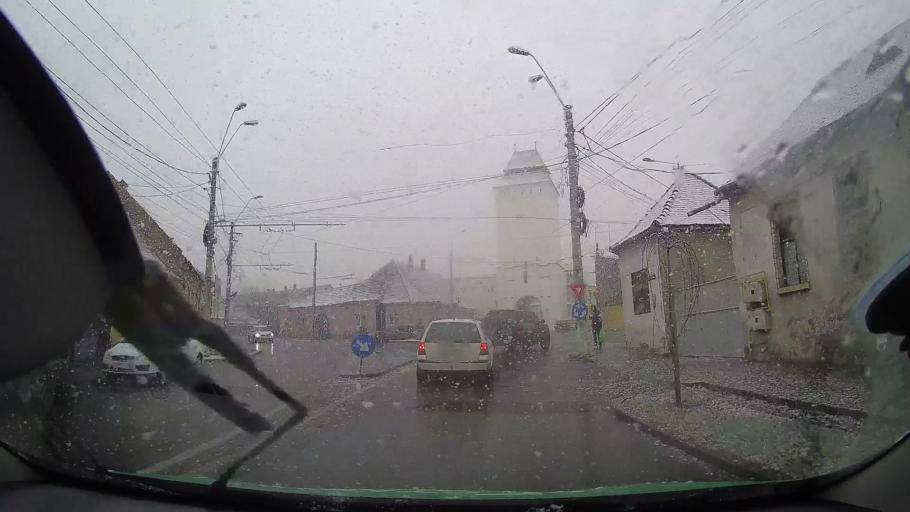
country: RO
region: Sibiu
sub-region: Municipiul Medias
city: Medias
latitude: 46.1691
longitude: 24.3493
